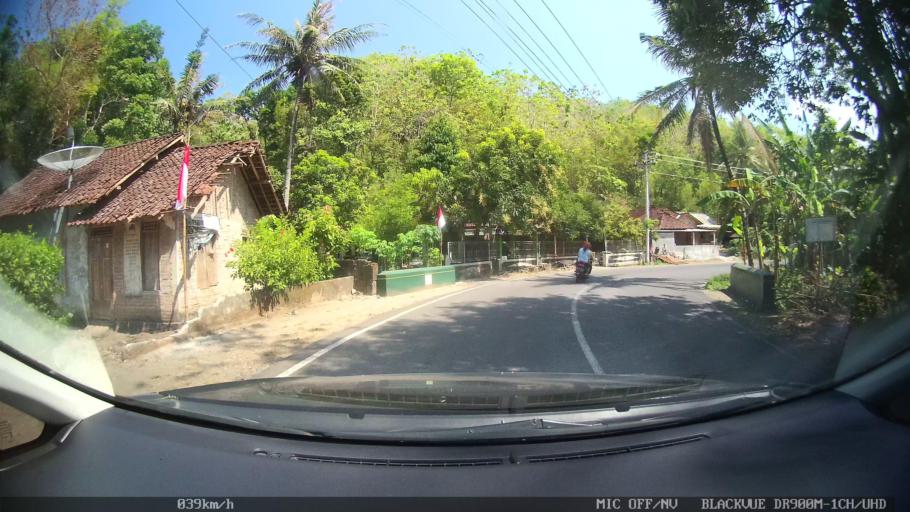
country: ID
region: Daerah Istimewa Yogyakarta
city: Pundong
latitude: -7.9588
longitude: 110.3805
